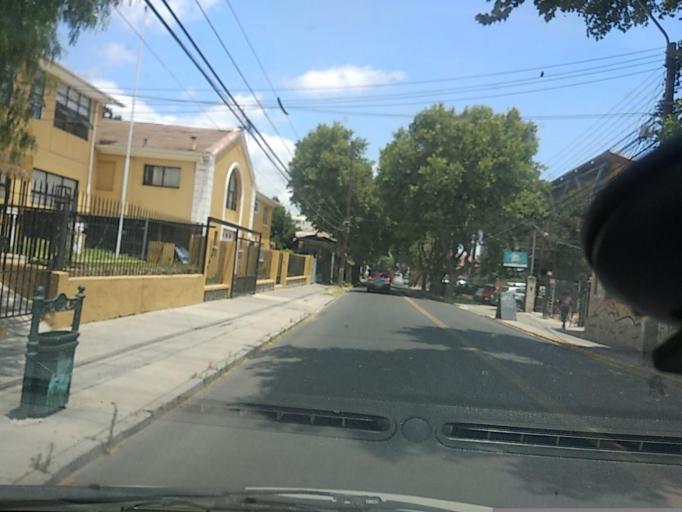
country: CL
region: Valparaiso
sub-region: Provincia de Marga Marga
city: Quilpue
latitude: -33.0454
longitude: -71.4389
